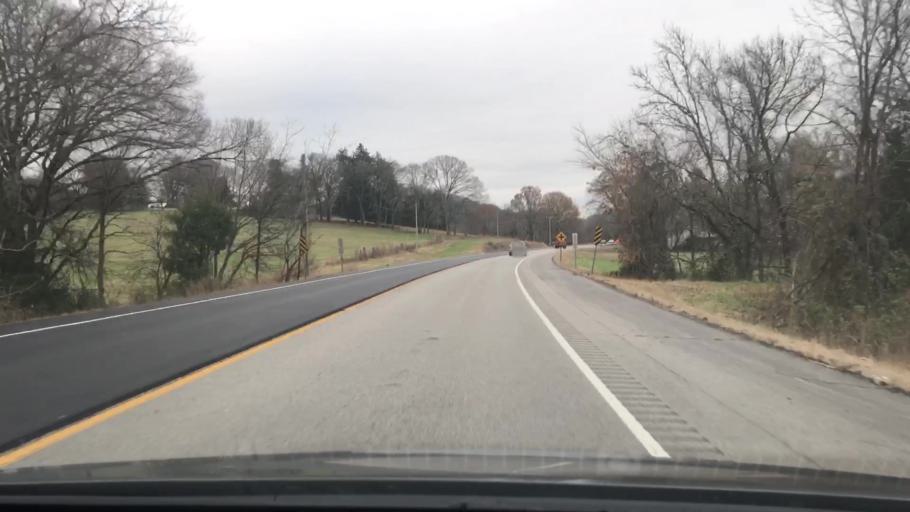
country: US
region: Tennessee
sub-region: Smith County
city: Carthage
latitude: 36.3175
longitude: -86.0112
